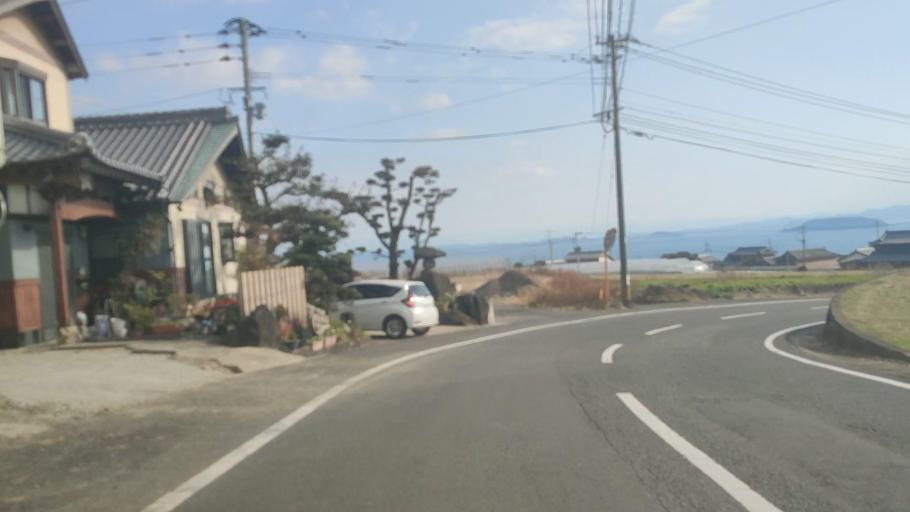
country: JP
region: Nagasaki
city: Shimabara
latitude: 32.6695
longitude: 130.2857
